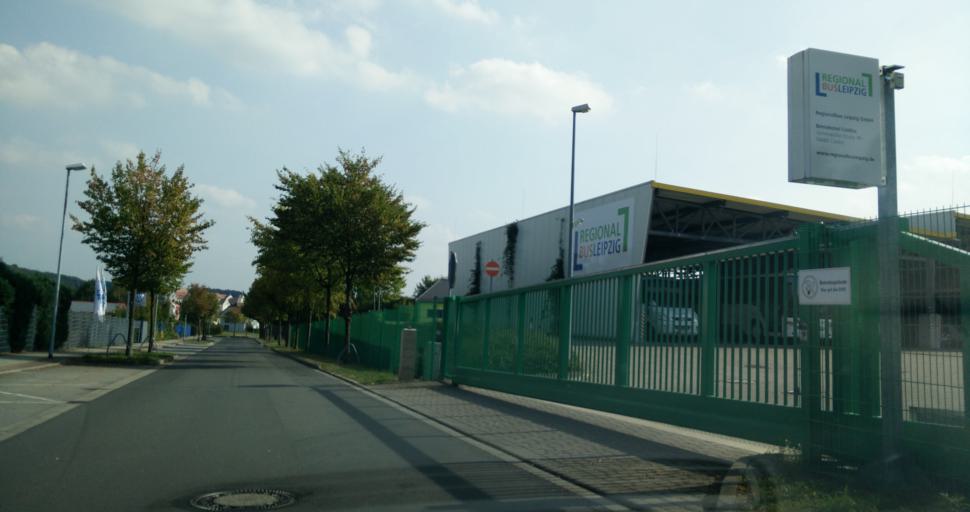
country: DE
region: Saxony
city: Colditz
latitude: 51.1363
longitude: 12.7916
